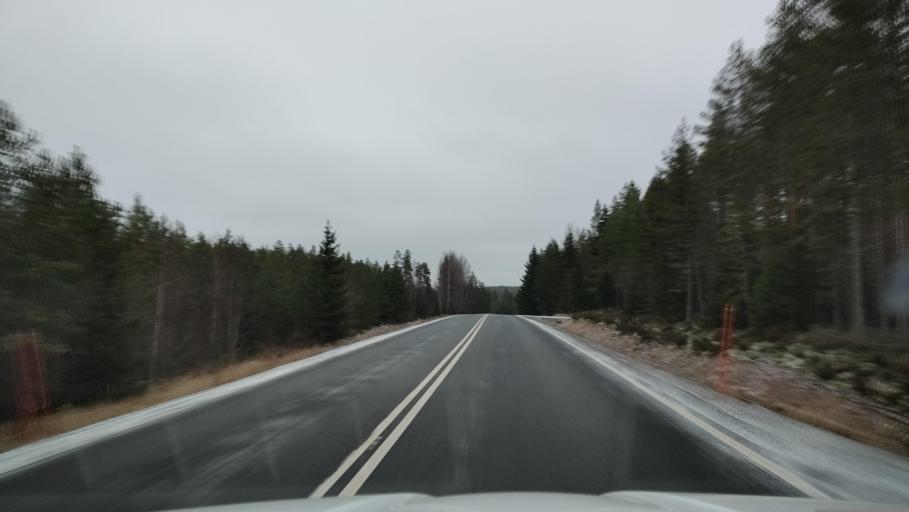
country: FI
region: Southern Ostrobothnia
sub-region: Suupohja
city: Karijoki
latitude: 62.2916
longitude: 21.6587
